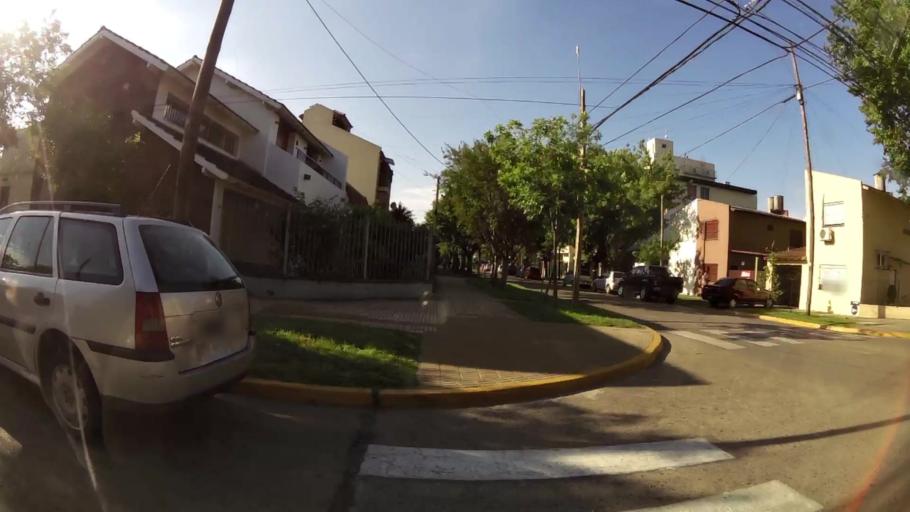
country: AR
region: Buenos Aires
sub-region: Partido de Merlo
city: Merlo
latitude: -34.6707
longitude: -58.7275
